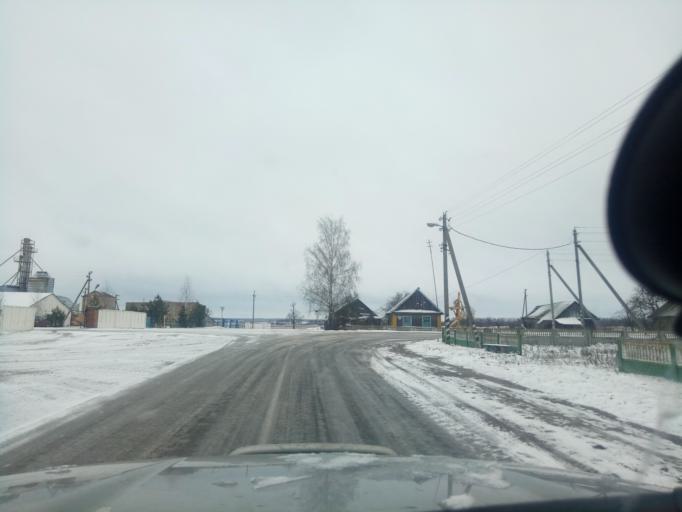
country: BY
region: Minsk
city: Klyetsk
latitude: 53.0508
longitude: 26.7439
